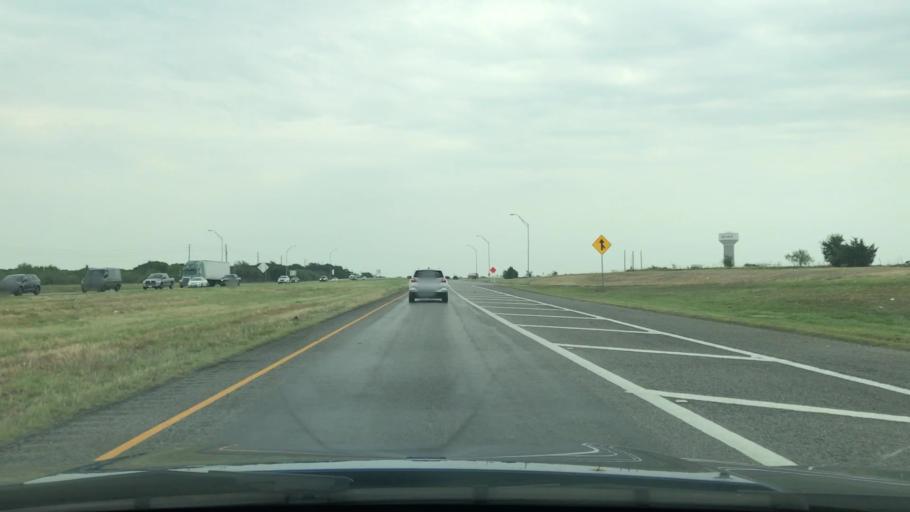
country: US
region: Texas
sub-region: Kaufman County
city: Terrell
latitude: 32.7199
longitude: -96.3179
